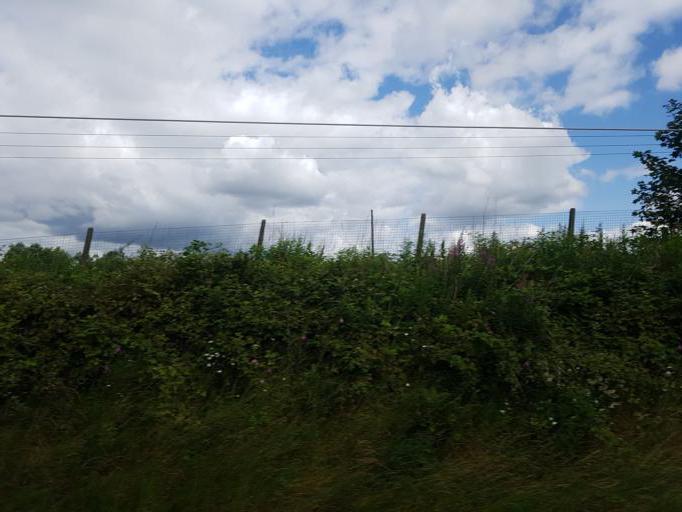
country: GB
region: Scotland
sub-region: Falkirk
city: Polmont
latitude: 55.9781
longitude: -3.6612
